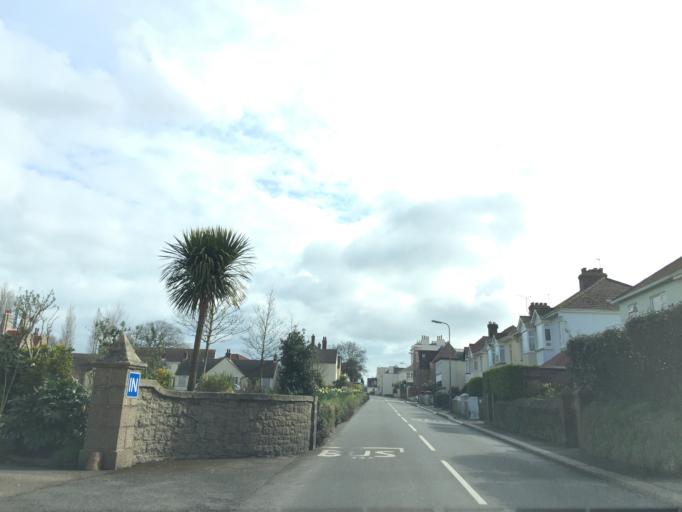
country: JE
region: St Helier
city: Saint Helier
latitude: 49.1975
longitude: -2.0851
